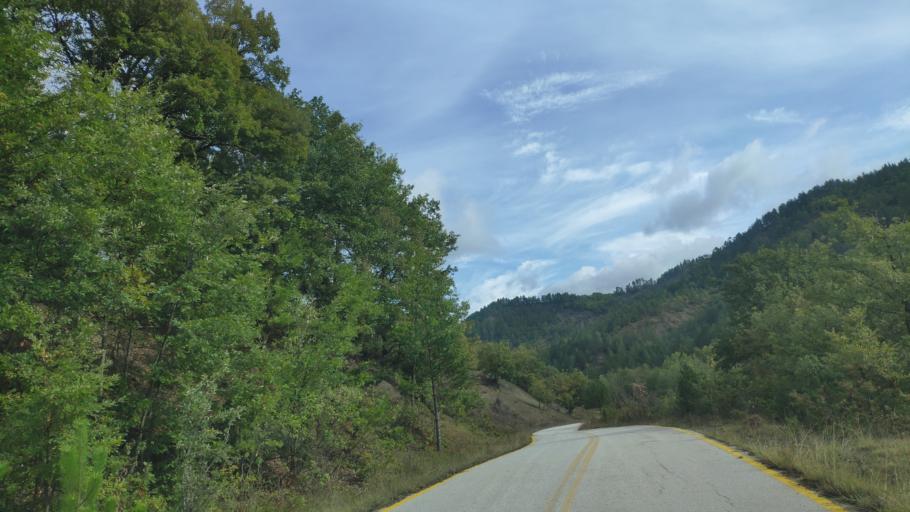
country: GR
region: West Macedonia
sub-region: Nomos Kastorias
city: Nestorio
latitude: 40.2327
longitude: 20.9876
